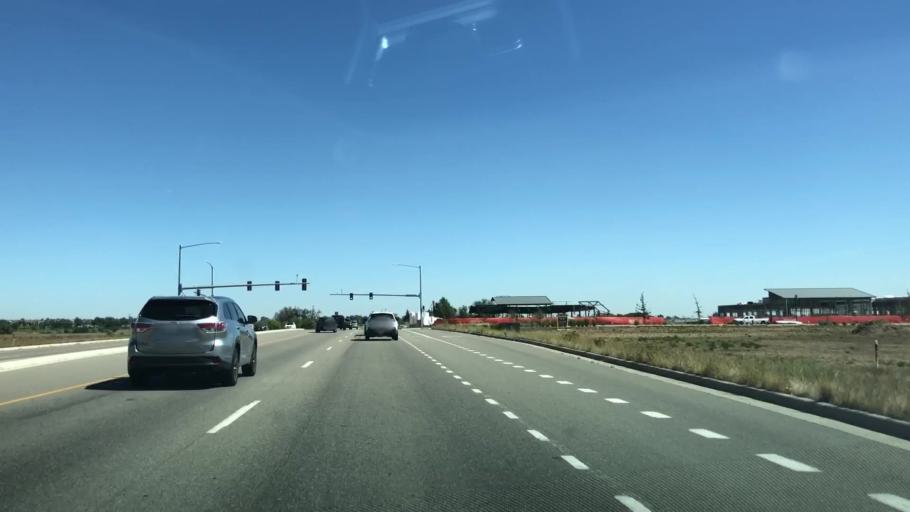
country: US
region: Colorado
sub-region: Weld County
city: Windsor
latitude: 40.5229
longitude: -104.9785
